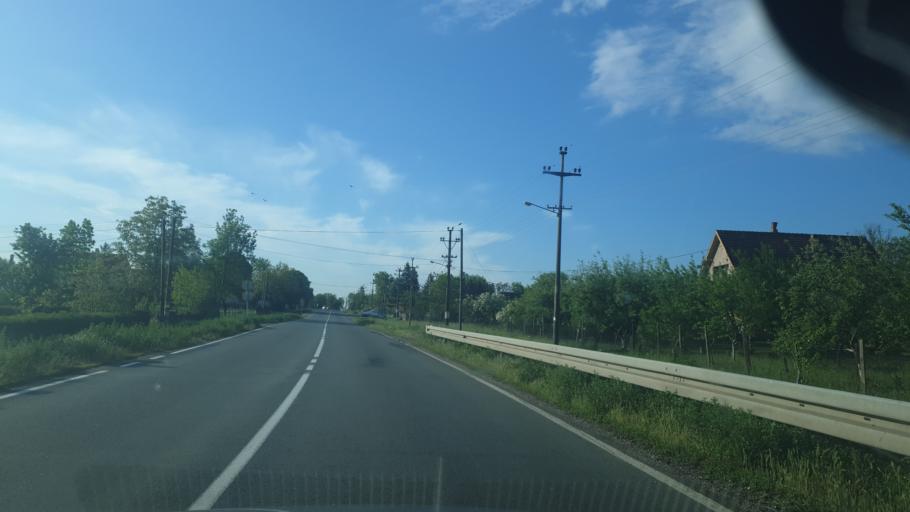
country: RS
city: Stubline
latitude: 44.5947
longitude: 20.1453
